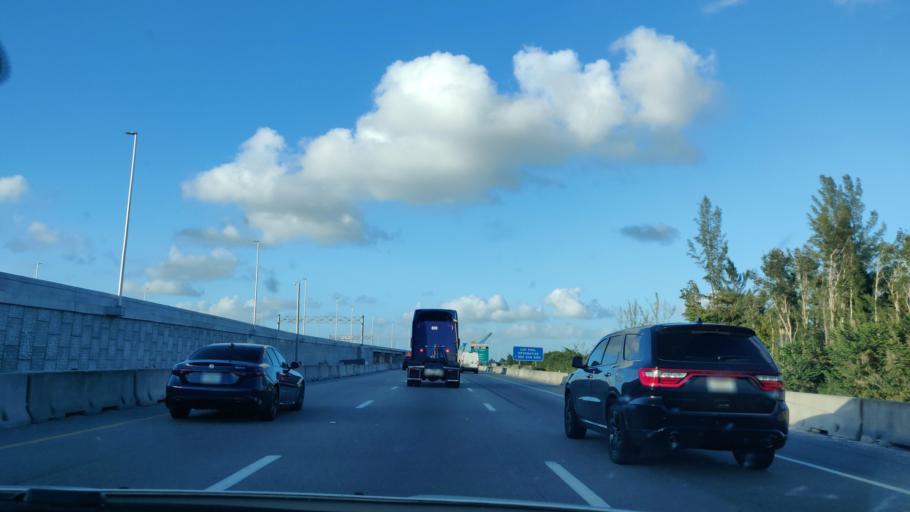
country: US
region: Florida
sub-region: Miami-Dade County
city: Palm Springs North
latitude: 25.9248
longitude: -80.3761
